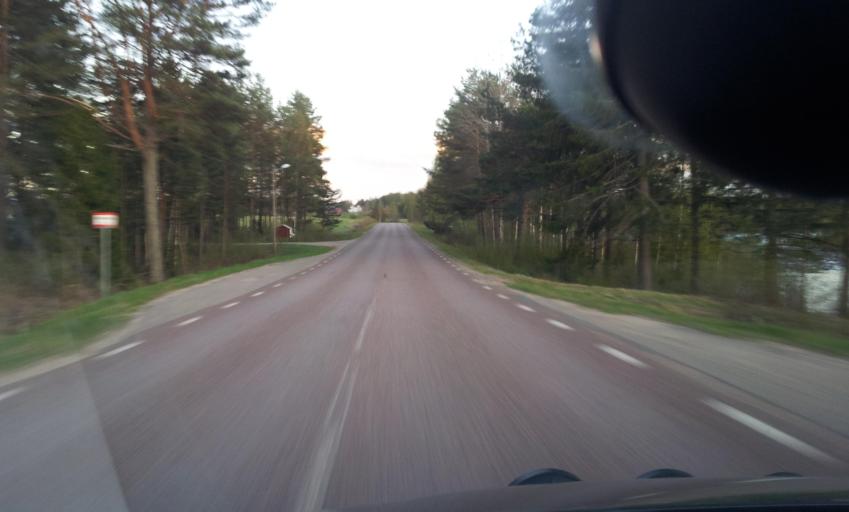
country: SE
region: Gaevleborg
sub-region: Bollnas Kommun
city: Bollnas
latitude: 61.3851
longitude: 16.4006
